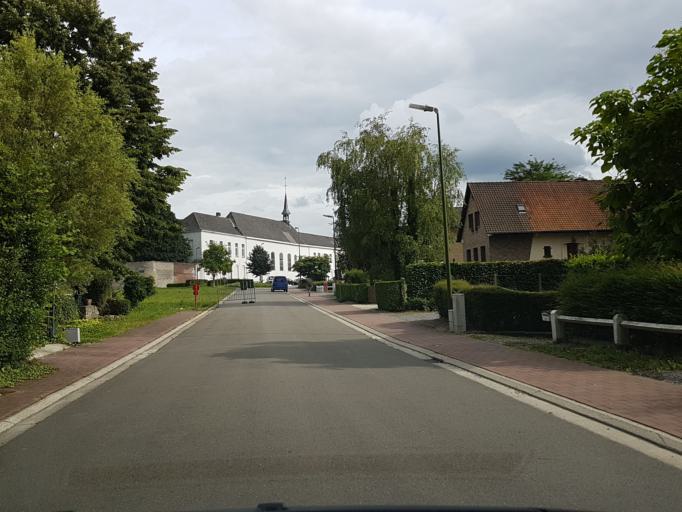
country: BE
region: Flanders
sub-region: Provincie Vlaams-Brabant
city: Steenokkerzeel
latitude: 50.9204
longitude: 4.4763
